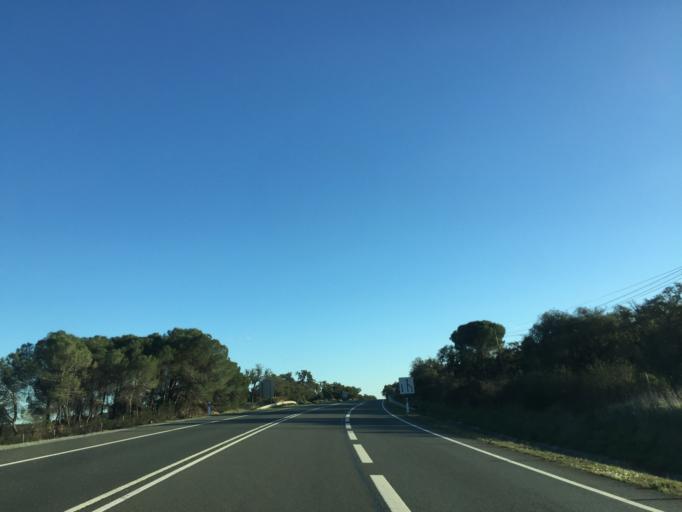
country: PT
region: Setubal
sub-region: Grandola
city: Grandola
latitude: 38.0582
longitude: -8.4051
